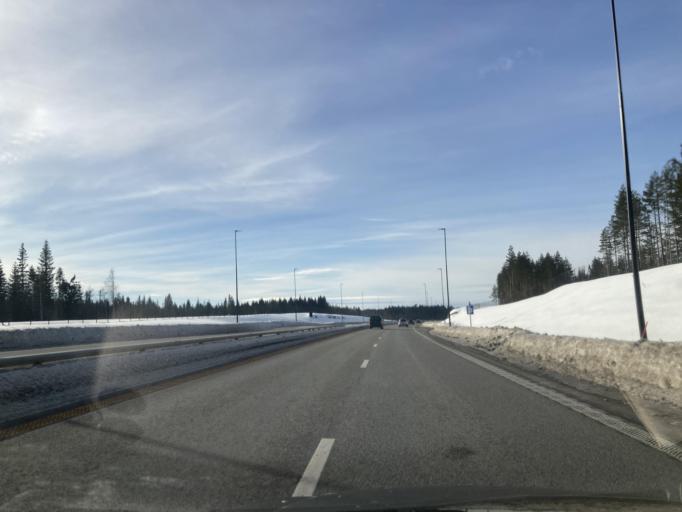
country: NO
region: Hedmark
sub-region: Loten
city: Loten
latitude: 60.8690
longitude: 11.4385
